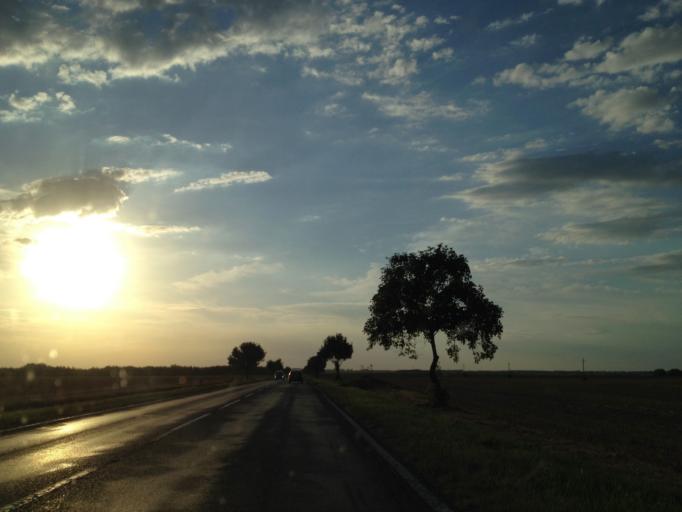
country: HU
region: Gyor-Moson-Sopron
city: Kimle
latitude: 47.7863
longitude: 17.4084
